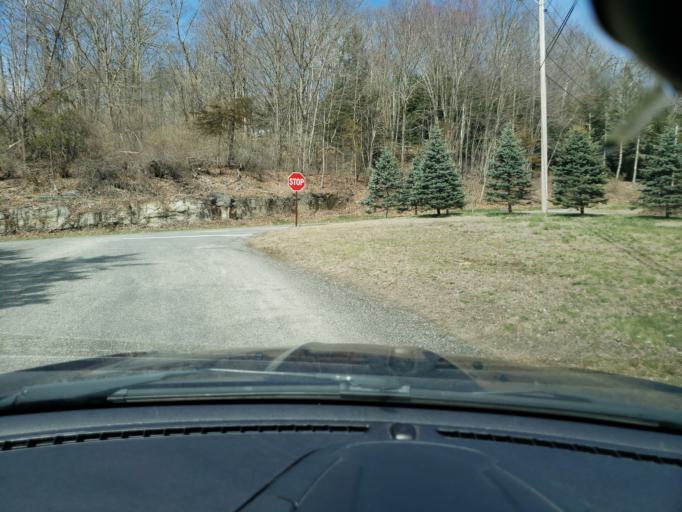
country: US
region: Connecticut
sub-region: Windham County
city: South Windham
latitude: 41.5755
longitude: -72.2060
